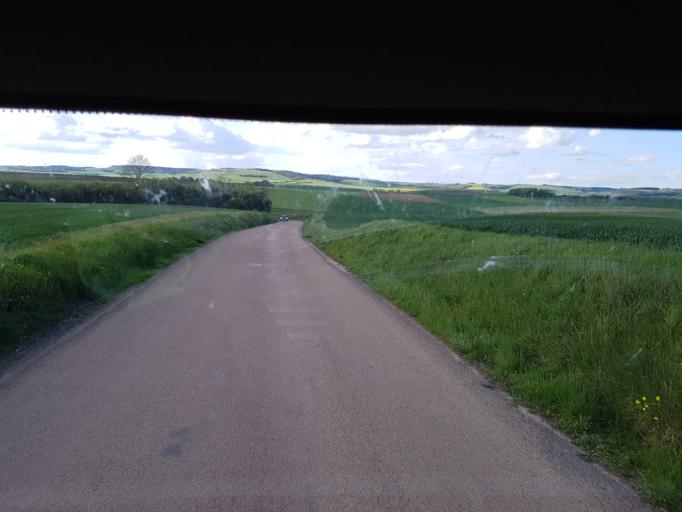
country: FR
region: Bourgogne
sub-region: Departement de l'Yonne
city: Neuvy-Sautour
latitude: 48.0464
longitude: 3.7901
